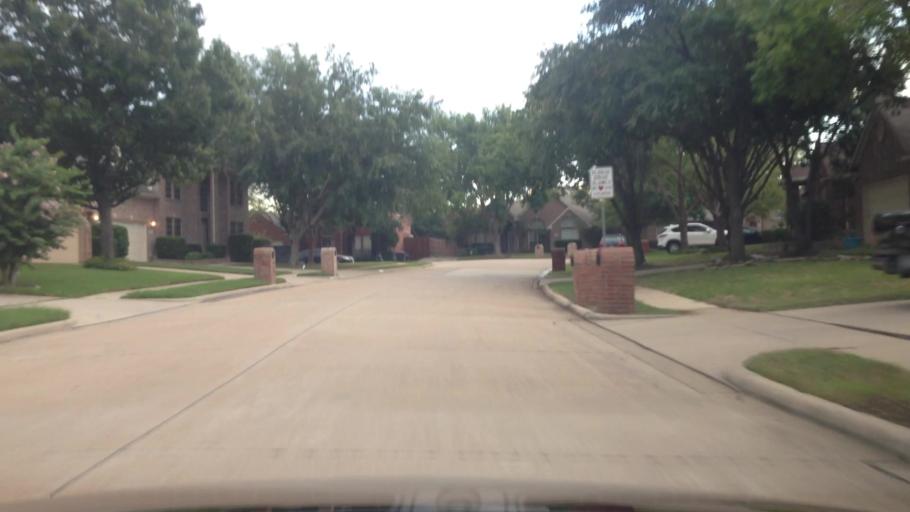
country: US
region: Texas
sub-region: Denton County
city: Flower Mound
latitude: 33.0019
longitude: -97.0539
